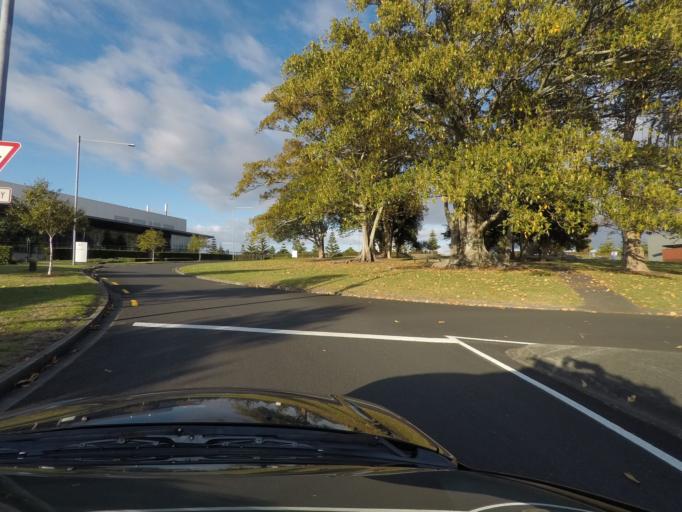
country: NZ
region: Auckland
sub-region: Auckland
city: Manukau City
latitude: -36.9418
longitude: 174.8701
